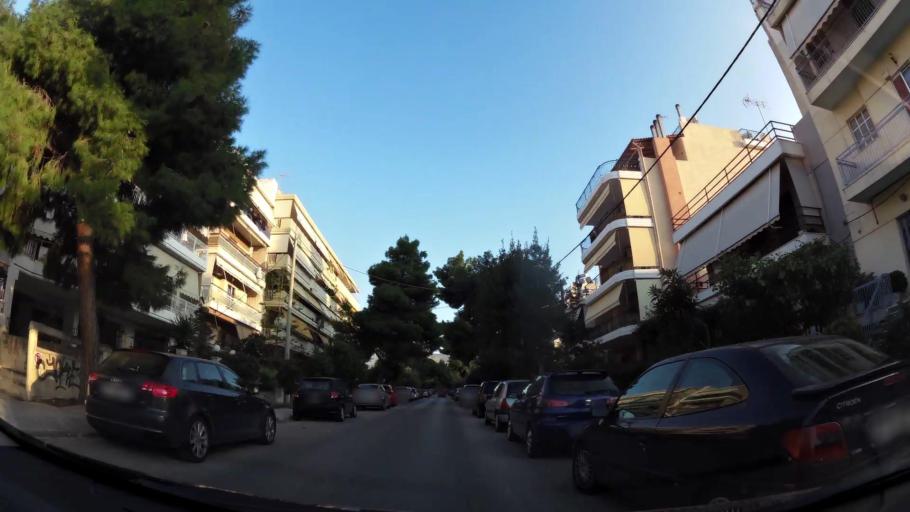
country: GR
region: Attica
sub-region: Nomarchia Athinas
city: Argyroupoli
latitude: 37.8890
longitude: 23.7643
